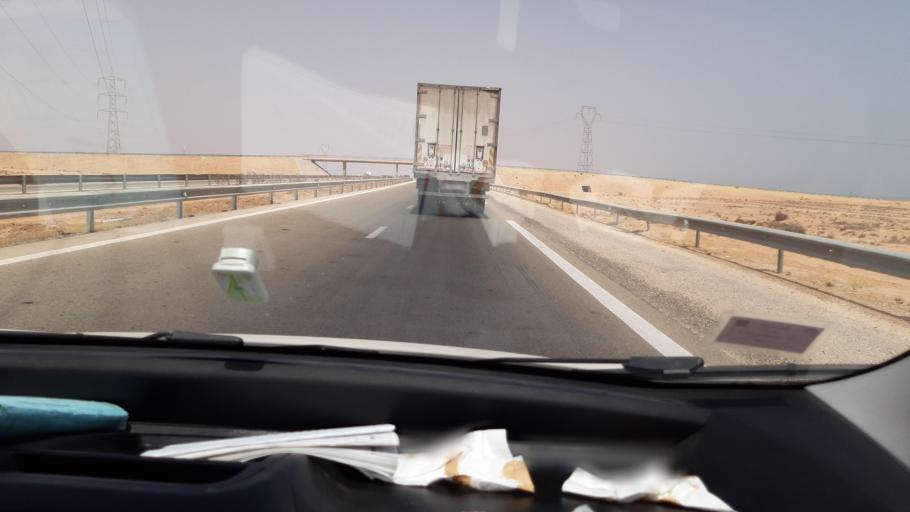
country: TN
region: Safaqis
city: Skhira
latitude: 34.1535
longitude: 9.9693
